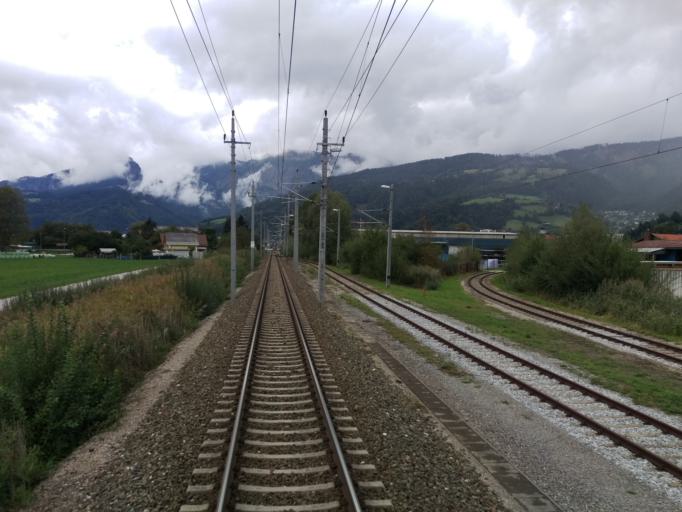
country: AT
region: Styria
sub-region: Politischer Bezirk Liezen
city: Liezen
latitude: 47.5584
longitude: 14.2504
